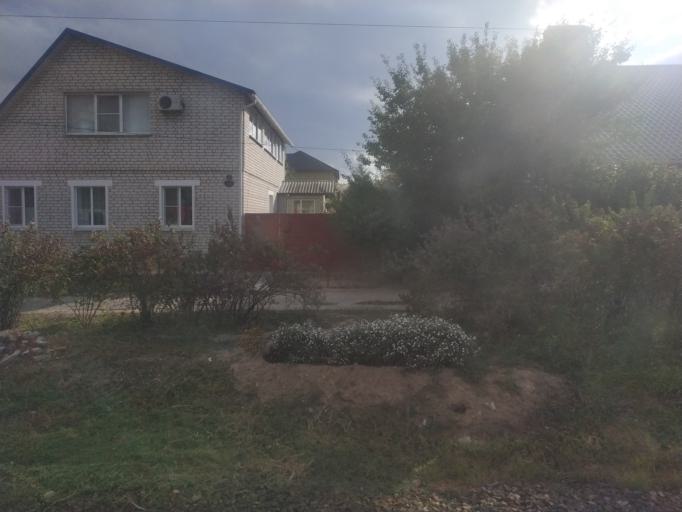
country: RU
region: Volgograd
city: Krasnoslobodsk
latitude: 48.5082
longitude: 44.5400
